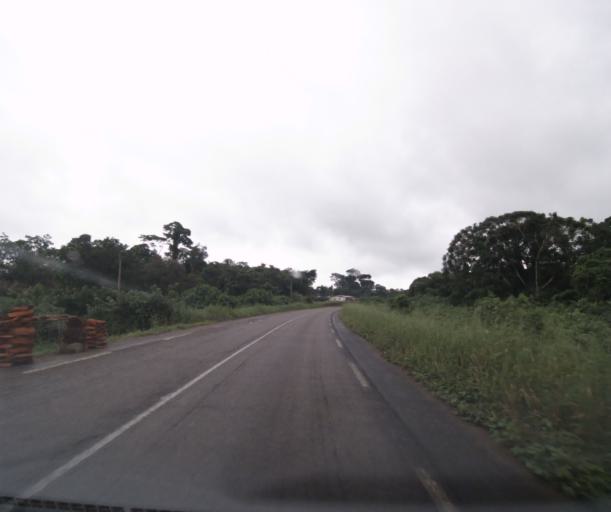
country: CM
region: Littoral
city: Dizangue
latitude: 3.5057
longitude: 10.1185
